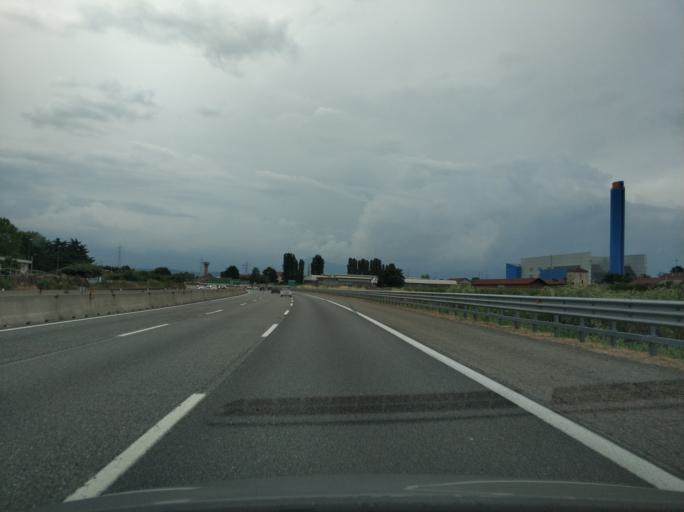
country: IT
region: Piedmont
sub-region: Provincia di Torino
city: Beinasco
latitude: 45.0315
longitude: 7.5896
